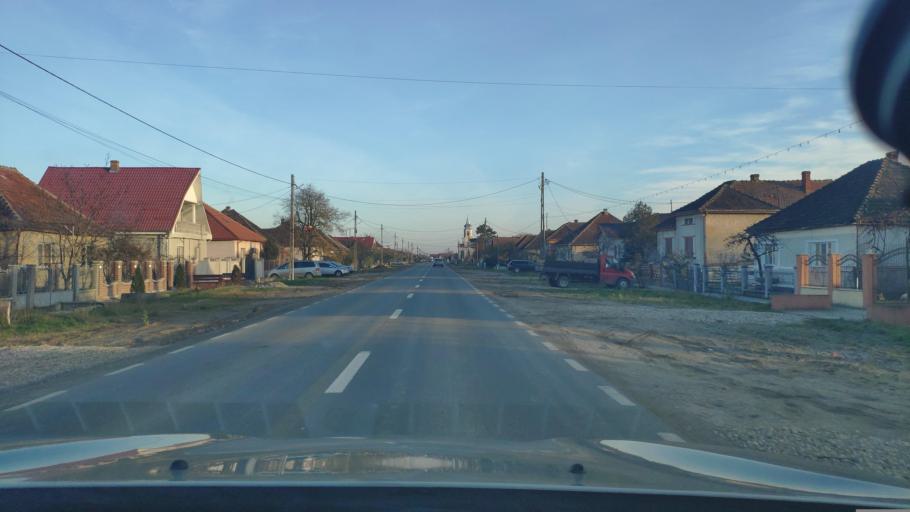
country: RO
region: Satu Mare
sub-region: Comuna Mediesu Aurit
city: Potau
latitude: 47.7780
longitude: 23.0908
